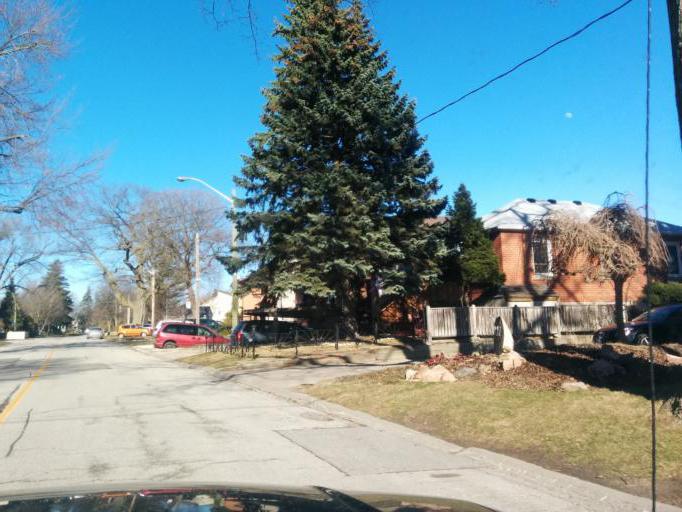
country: CA
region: Ontario
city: Etobicoke
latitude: 43.5865
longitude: -79.5404
